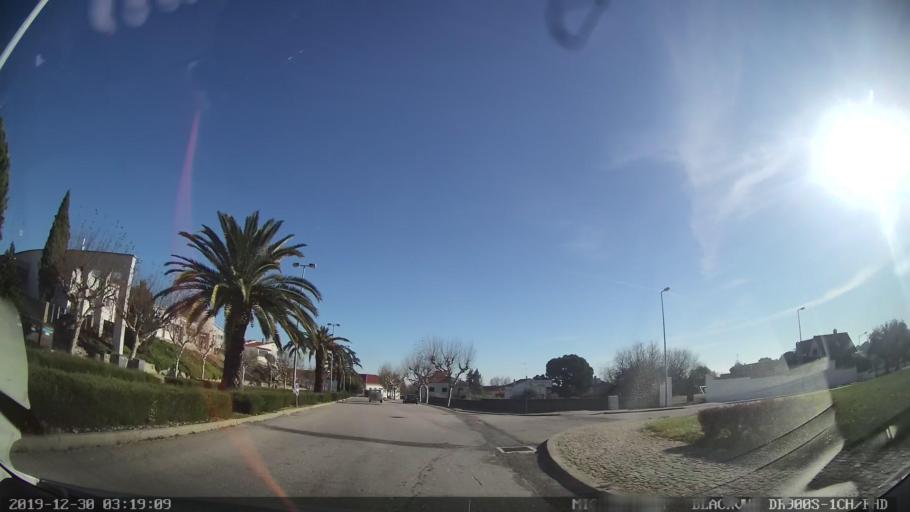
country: PT
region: Castelo Branco
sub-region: Idanha-A-Nova
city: Idanha-a-Nova
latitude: 39.9244
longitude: -7.2436
